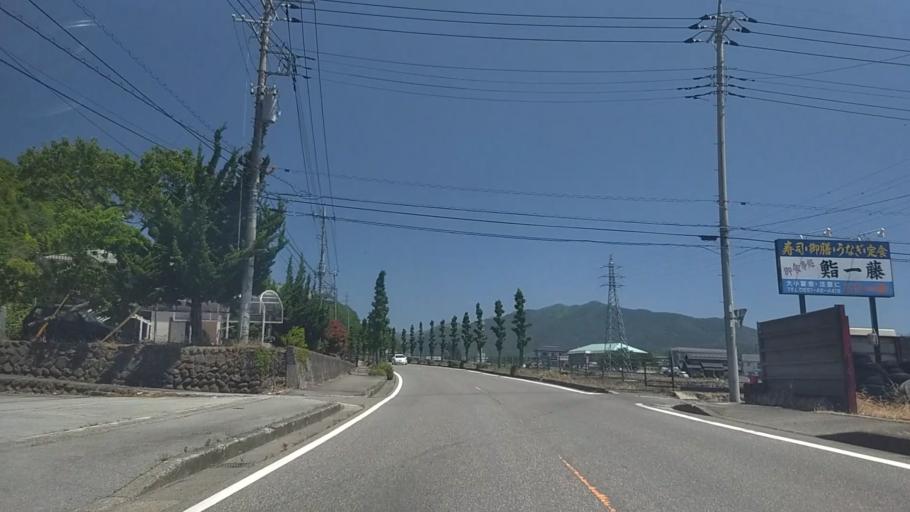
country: JP
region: Yamanashi
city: Nirasaki
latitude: 35.7971
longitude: 138.4242
